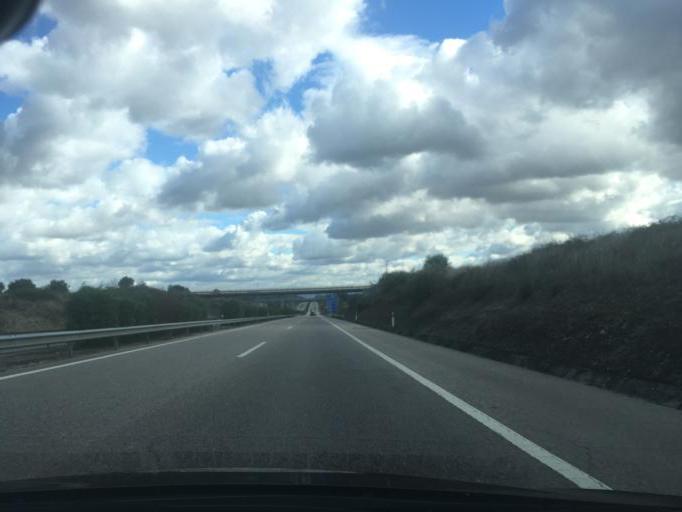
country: PT
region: Santarem
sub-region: Torres Novas
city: Torres Novas
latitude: 39.4719
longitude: -8.5771
